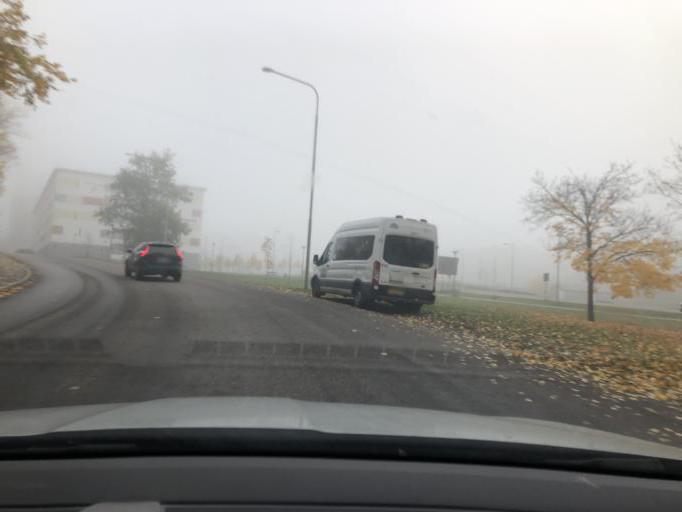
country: SE
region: Stockholm
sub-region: Botkyrka Kommun
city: Tullinge
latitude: 59.2244
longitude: 17.9348
